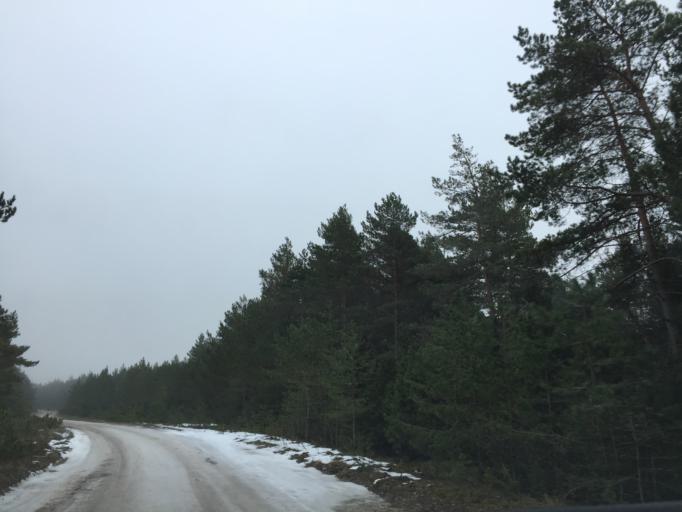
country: EE
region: Saare
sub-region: Kuressaare linn
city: Kuressaare
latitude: 58.5062
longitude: 21.9594
